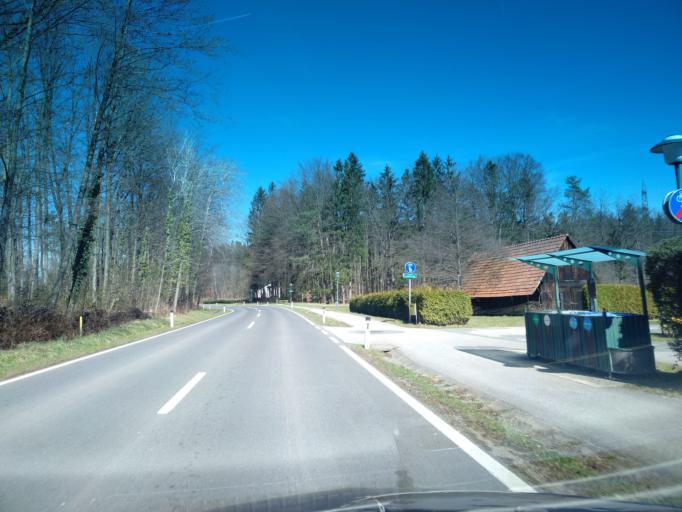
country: AT
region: Styria
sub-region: Politischer Bezirk Deutschlandsberg
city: Hollenegg
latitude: 46.7890
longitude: 15.2370
